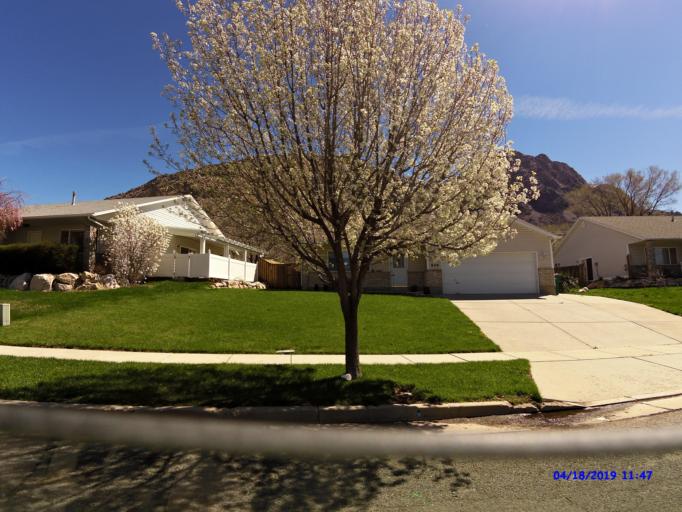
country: US
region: Utah
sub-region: Weber County
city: North Ogden
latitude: 41.2728
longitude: -111.9535
